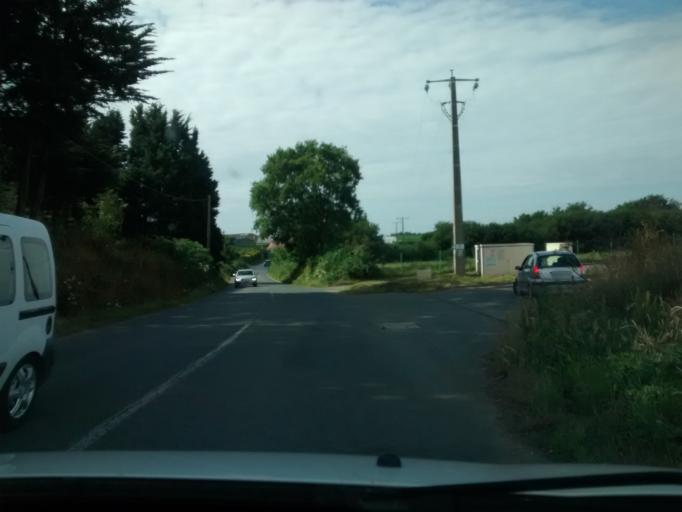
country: FR
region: Brittany
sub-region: Departement des Cotes-d'Armor
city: Penvenan
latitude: 48.7954
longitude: -3.2883
